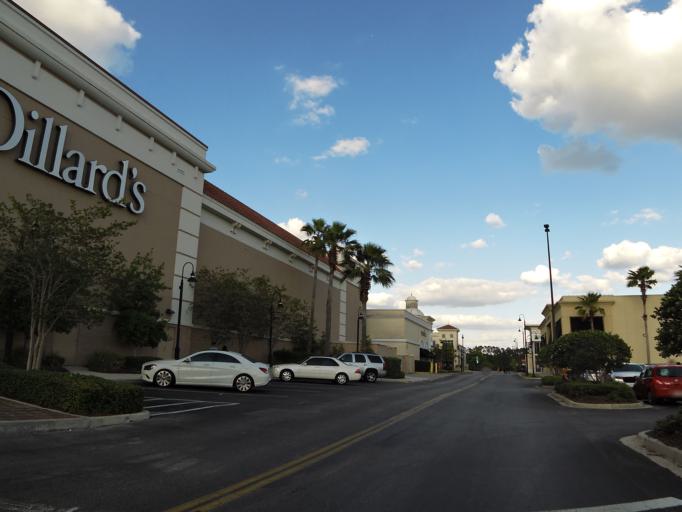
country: US
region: Florida
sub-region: Duval County
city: Jacksonville Beach
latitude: 30.2555
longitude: -81.5266
